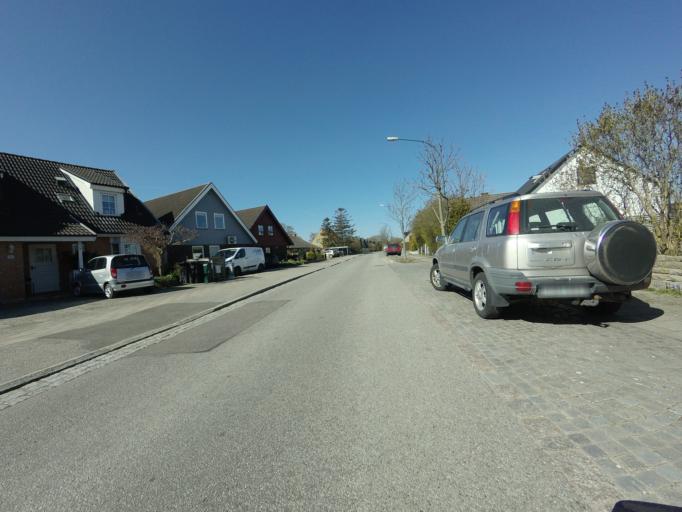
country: SE
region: Skane
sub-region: Trelleborgs Kommun
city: Trelleborg
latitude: 55.3774
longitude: 13.1096
